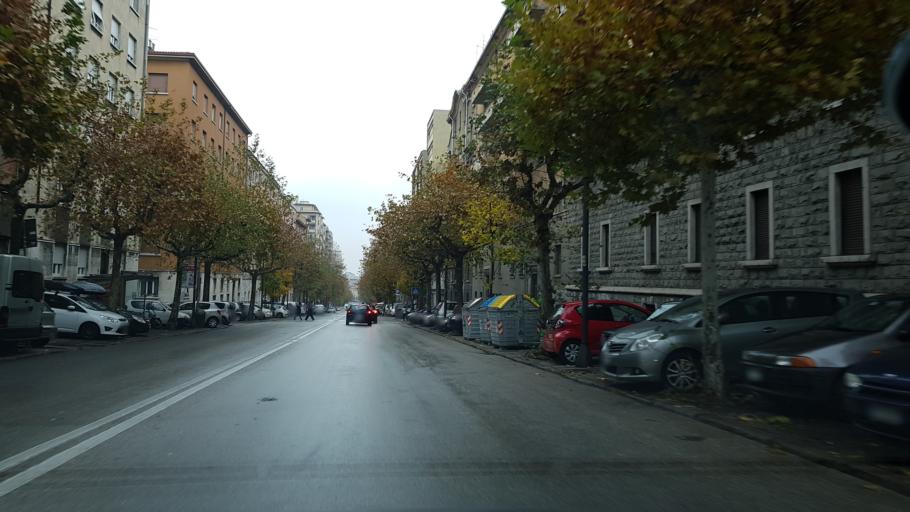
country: IT
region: Friuli Venezia Giulia
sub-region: Provincia di Trieste
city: Trieste
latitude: 45.6408
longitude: 13.7871
